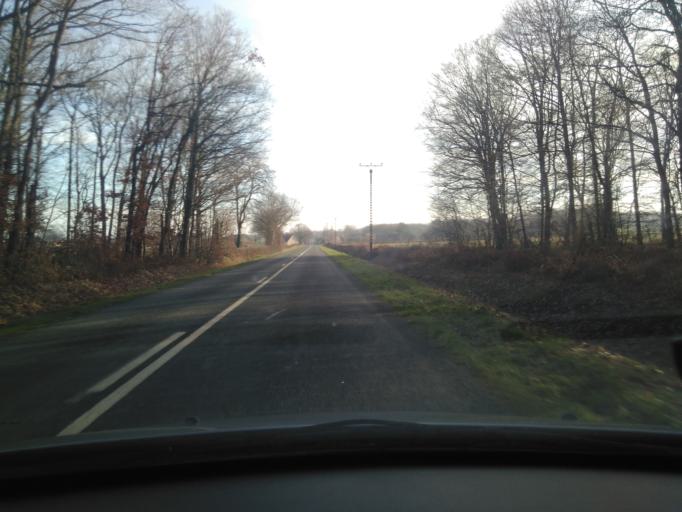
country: FR
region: Centre
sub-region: Departement du Cher
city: Chateaumeillant
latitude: 46.6372
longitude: 2.1112
